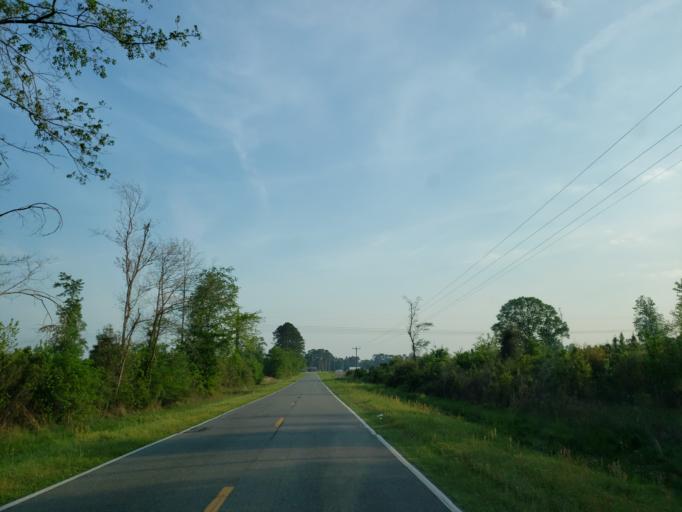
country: US
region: Georgia
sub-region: Cook County
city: Sparks
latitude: 31.2078
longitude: -83.4220
